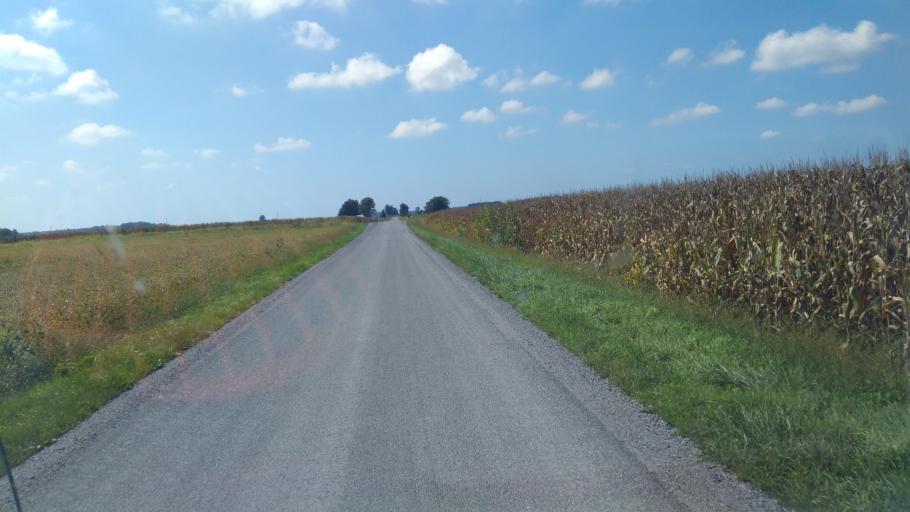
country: US
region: Ohio
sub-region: Hardin County
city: Ada
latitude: 40.7618
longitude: -83.7414
